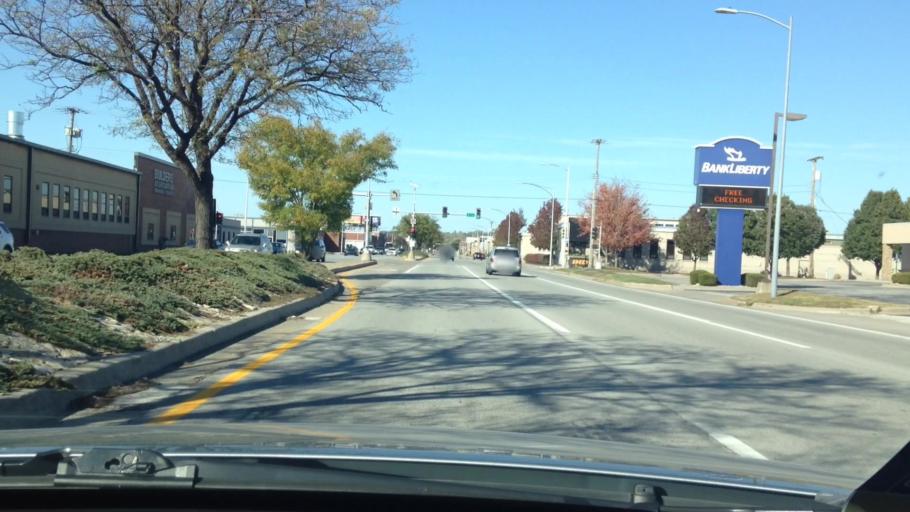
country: US
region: Missouri
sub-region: Clay County
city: North Kansas City
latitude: 39.1297
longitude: -94.5806
